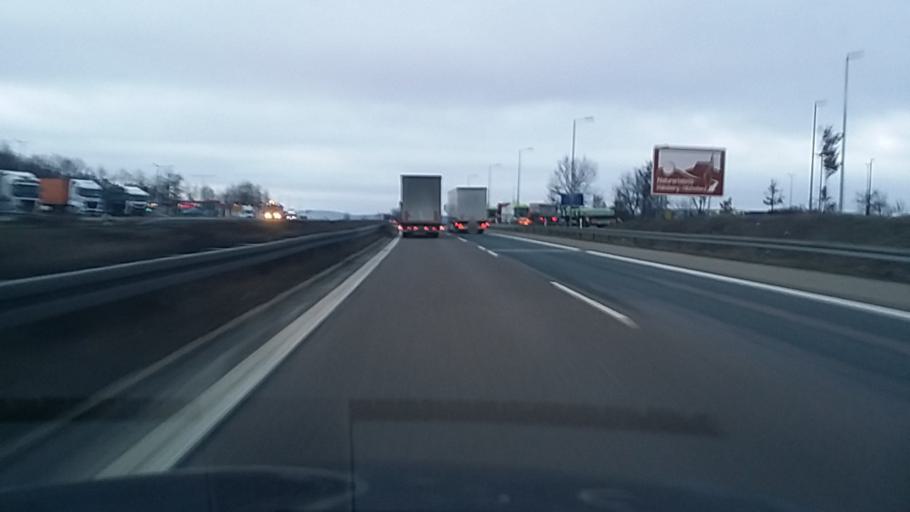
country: DE
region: Bavaria
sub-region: Upper Palatinate
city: Deining
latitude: 49.2707
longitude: 11.6016
